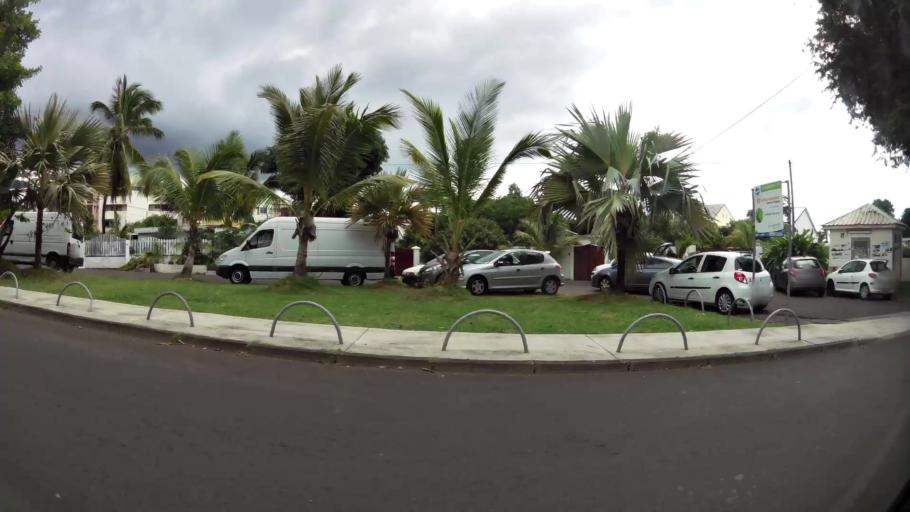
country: RE
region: Reunion
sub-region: Reunion
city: Saint-Denis
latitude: -20.8898
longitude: 55.4742
